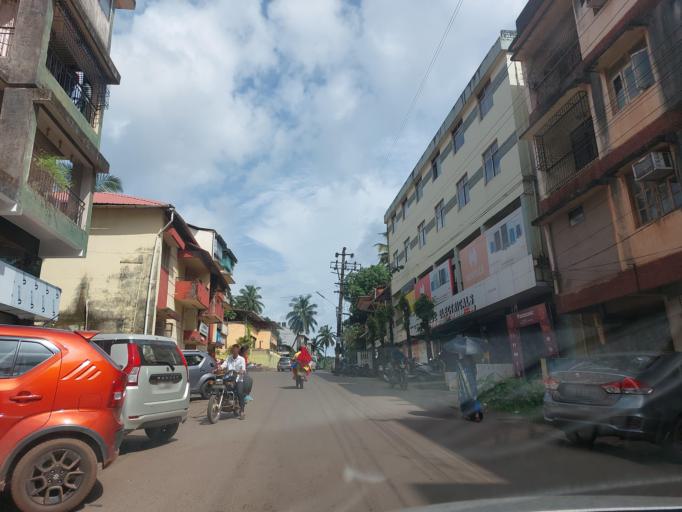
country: IN
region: Goa
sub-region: North Goa
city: Ponda
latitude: 15.3996
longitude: 74.0058
